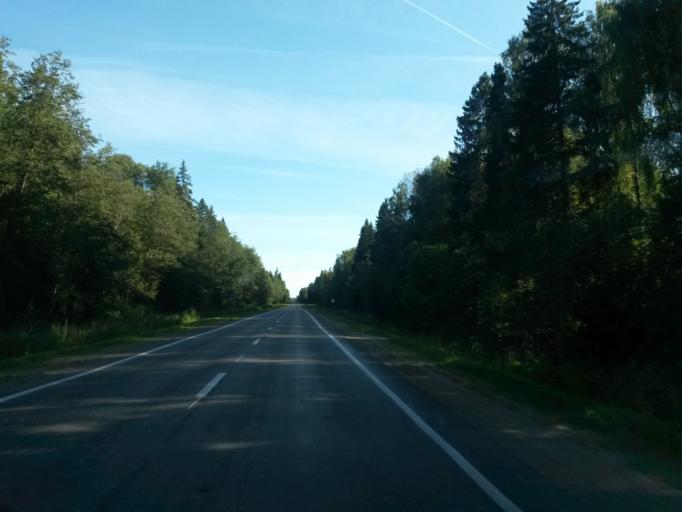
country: RU
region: Jaroslavl
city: Gavrilov-Yam
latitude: 57.4296
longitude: 39.9185
